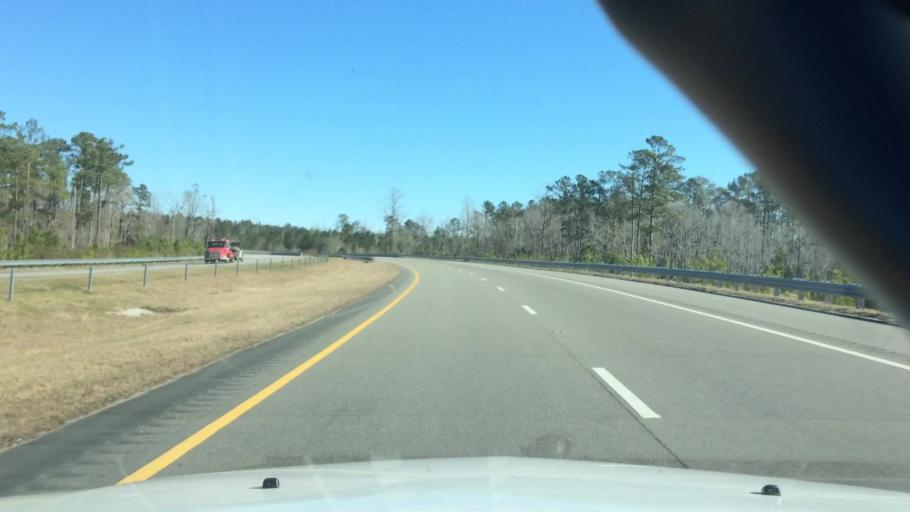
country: US
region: North Carolina
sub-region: Brunswick County
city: Leland
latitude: 34.2063
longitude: -78.0791
